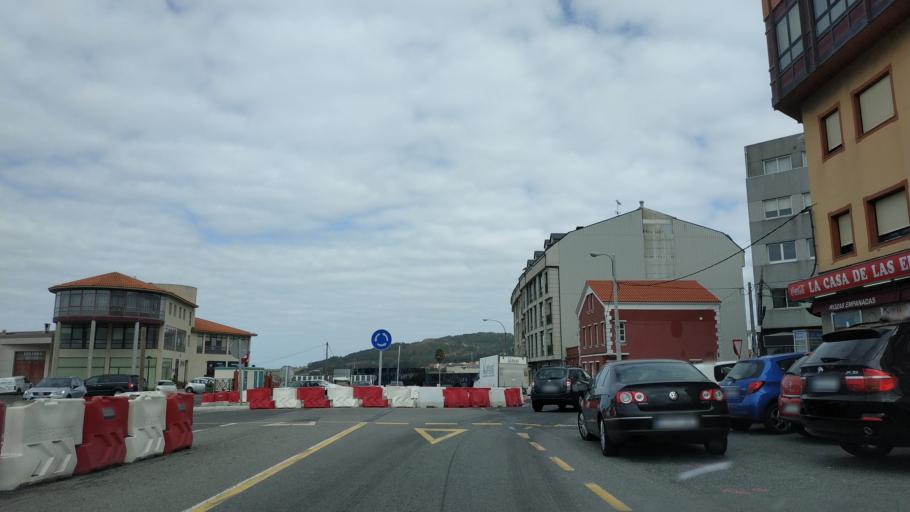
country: ES
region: Galicia
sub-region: Provincia da Coruna
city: Arteixo
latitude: 43.3144
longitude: -8.5003
